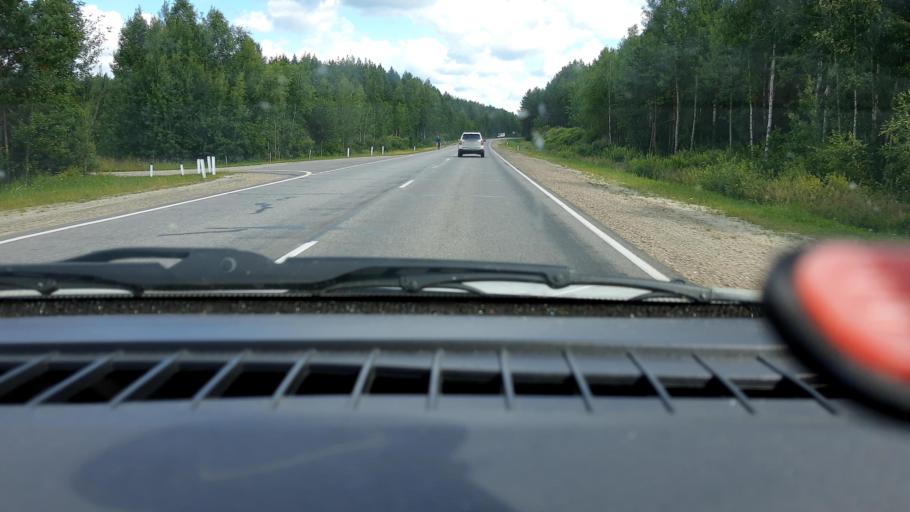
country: RU
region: Nizjnij Novgorod
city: Arzamas
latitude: 55.3577
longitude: 43.8949
